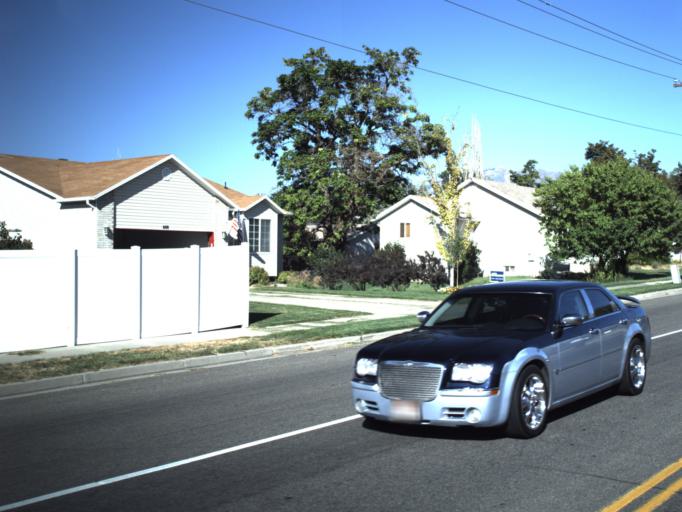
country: US
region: Utah
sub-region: Davis County
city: Sunset
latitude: 41.1399
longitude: -112.0396
